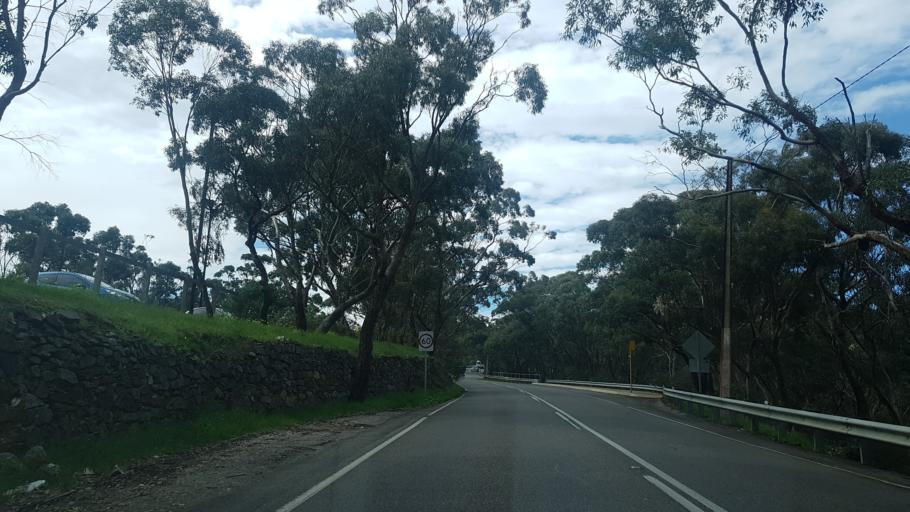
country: AU
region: South Australia
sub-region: Mitcham
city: Clapham
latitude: -35.0006
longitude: 138.6070
